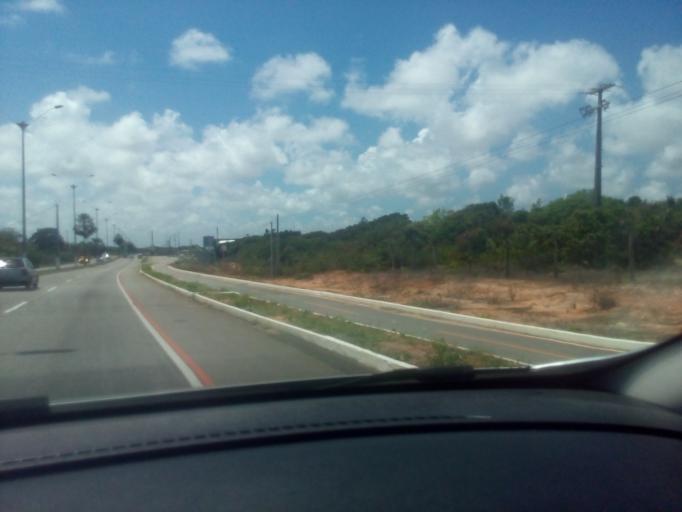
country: BR
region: Rio Grande do Norte
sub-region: Parnamirim
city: Parnamirim
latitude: -5.9205
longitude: -35.1680
